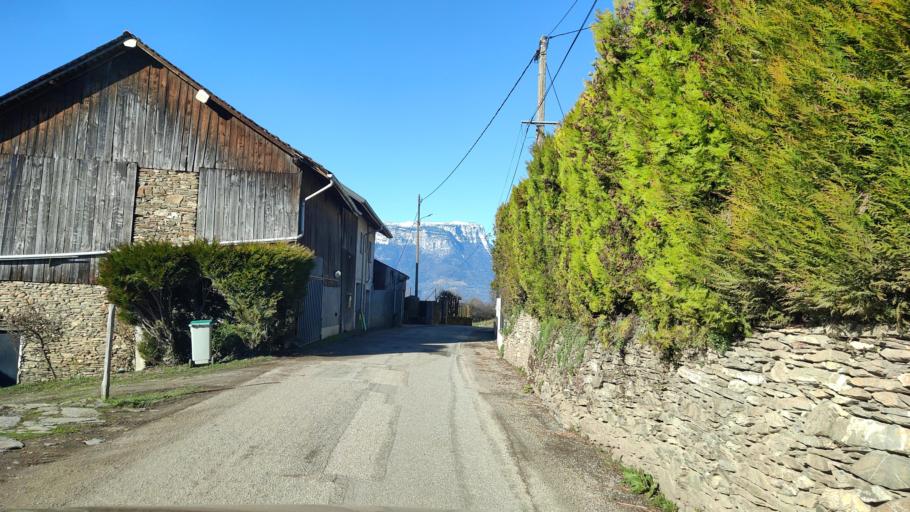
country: FR
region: Rhone-Alpes
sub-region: Departement de la Savoie
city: La Rochette
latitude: 45.4483
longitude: 6.0785
